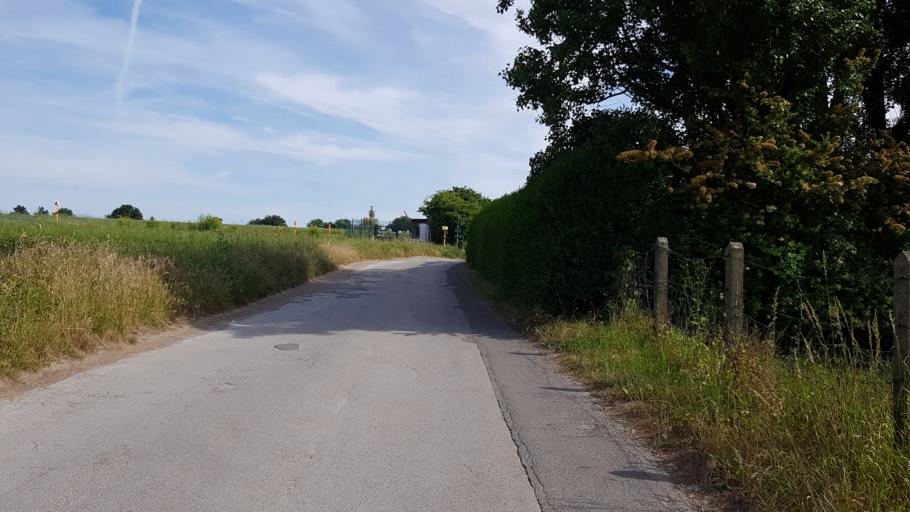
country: DE
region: North Rhine-Westphalia
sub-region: Regierungsbezirk Dusseldorf
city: Muelheim (Ruhr)
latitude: 51.4059
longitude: 6.9241
